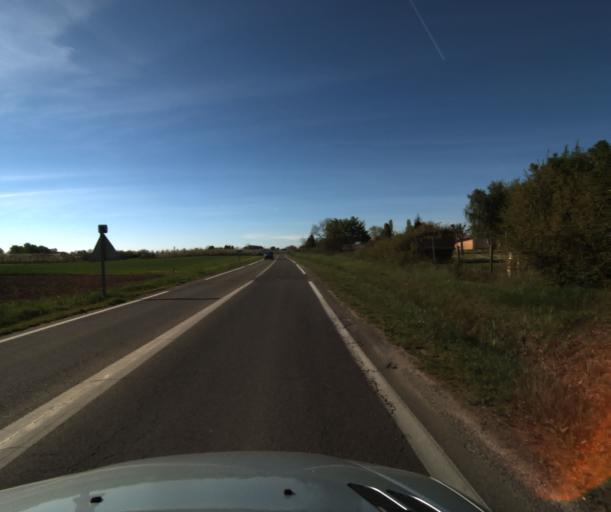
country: FR
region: Midi-Pyrenees
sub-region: Departement du Tarn-et-Garonne
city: Montbeton
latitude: 44.0336
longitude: 1.3141
